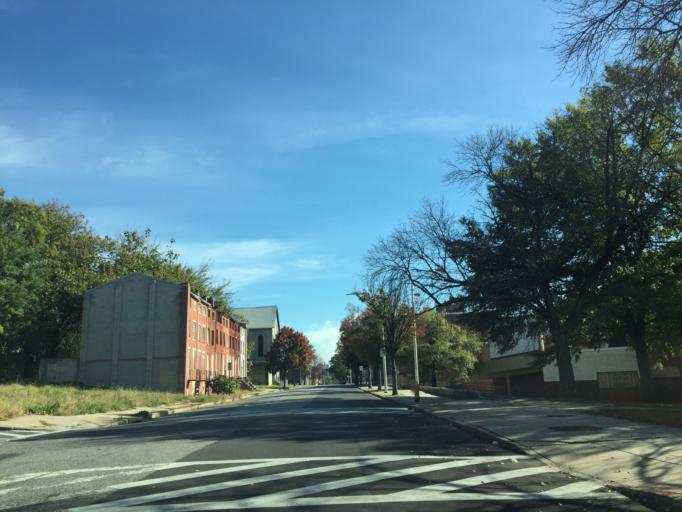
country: US
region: Maryland
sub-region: City of Baltimore
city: Baltimore
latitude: 39.2923
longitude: -76.6357
